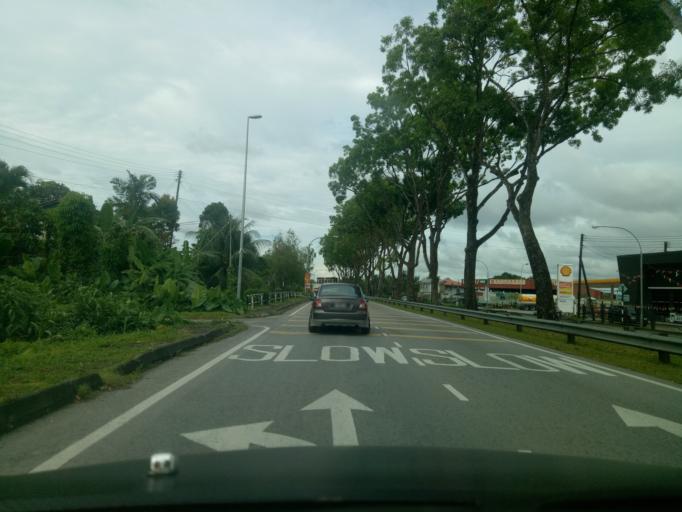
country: MY
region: Sarawak
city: Kuching
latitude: 1.5456
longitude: 110.3791
